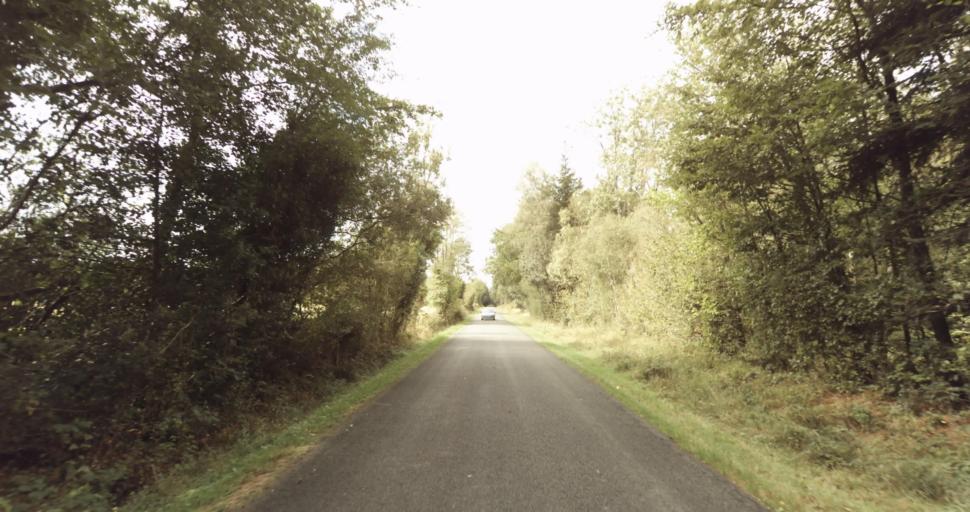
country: FR
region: Lower Normandy
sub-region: Departement de l'Orne
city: Sainte-Gauburge-Sainte-Colombe
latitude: 48.7794
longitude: 0.3885
